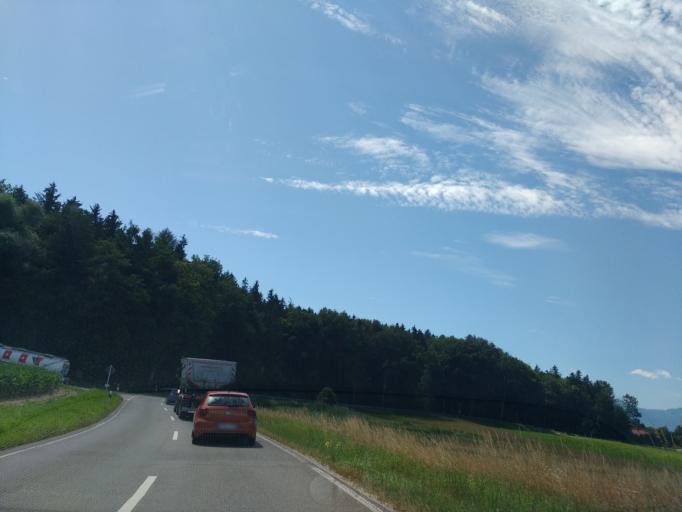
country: DE
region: Bavaria
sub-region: Upper Bavaria
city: Seeon-Seebruck
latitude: 47.9343
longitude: 12.4968
